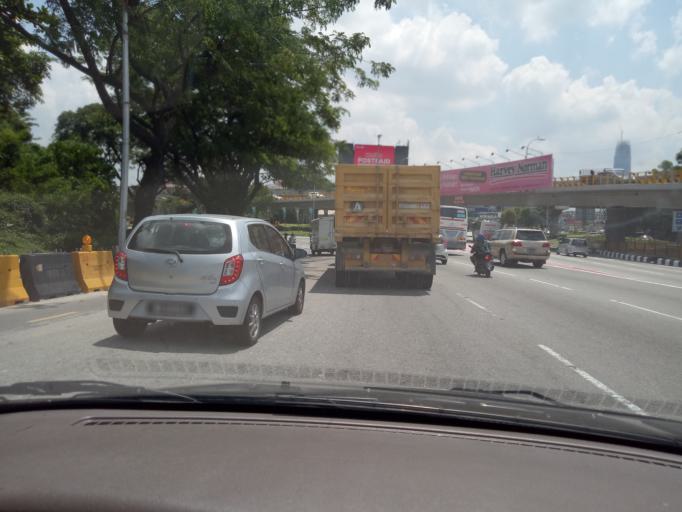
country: MY
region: Kuala Lumpur
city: Kuala Lumpur
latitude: 3.1210
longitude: 101.7080
